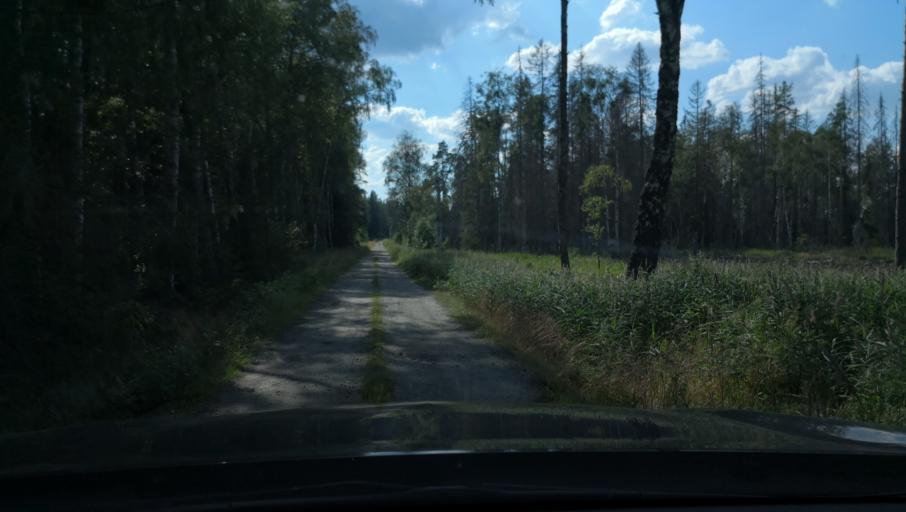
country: SE
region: Vaestmanland
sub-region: Vasteras
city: Skultuna
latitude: 59.7249
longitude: 16.3586
